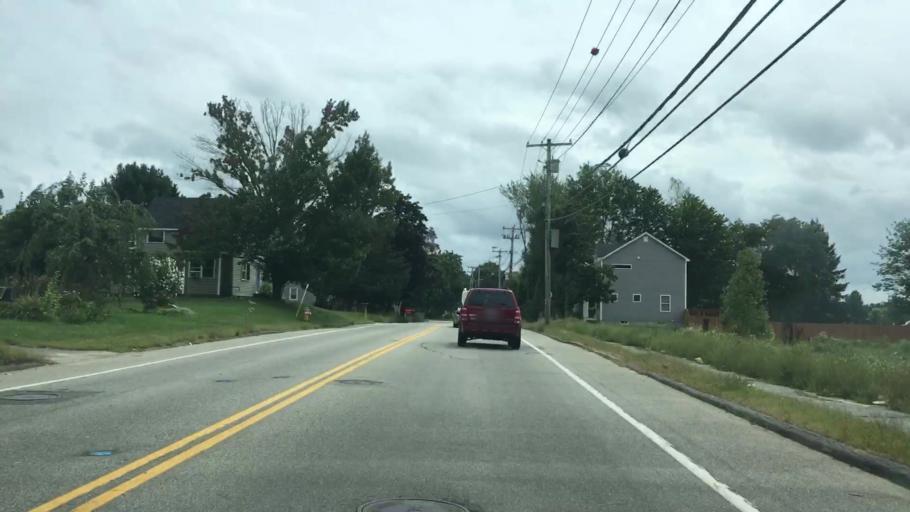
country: US
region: Maine
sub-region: Cumberland County
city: Westbrook
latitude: 43.6677
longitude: -70.3595
